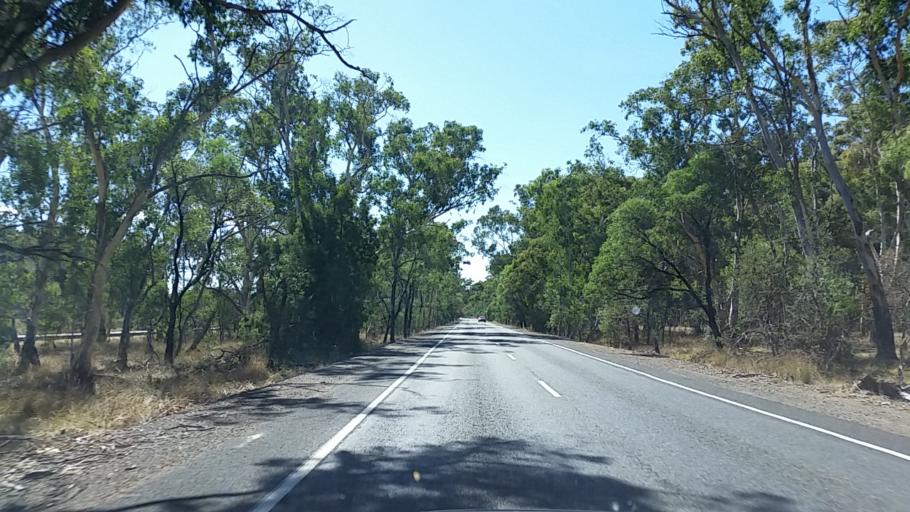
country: AU
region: South Australia
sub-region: Adelaide Hills
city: Birdwood
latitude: -34.7385
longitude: 138.9617
